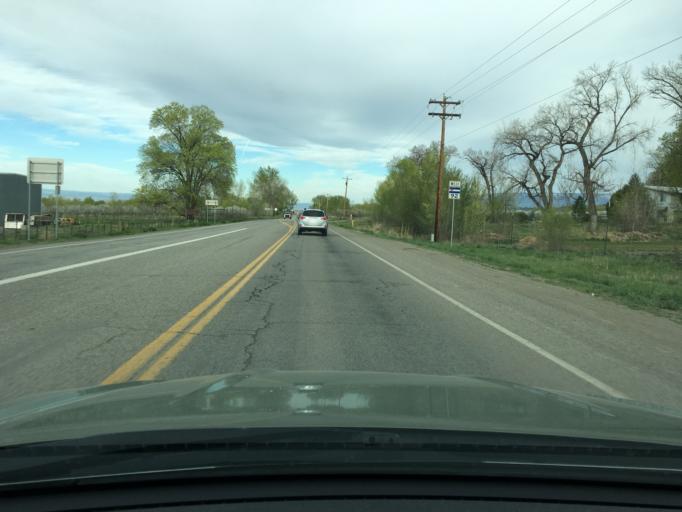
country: US
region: Colorado
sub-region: Delta County
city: Cedaredge
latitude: 38.8005
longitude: -107.7820
